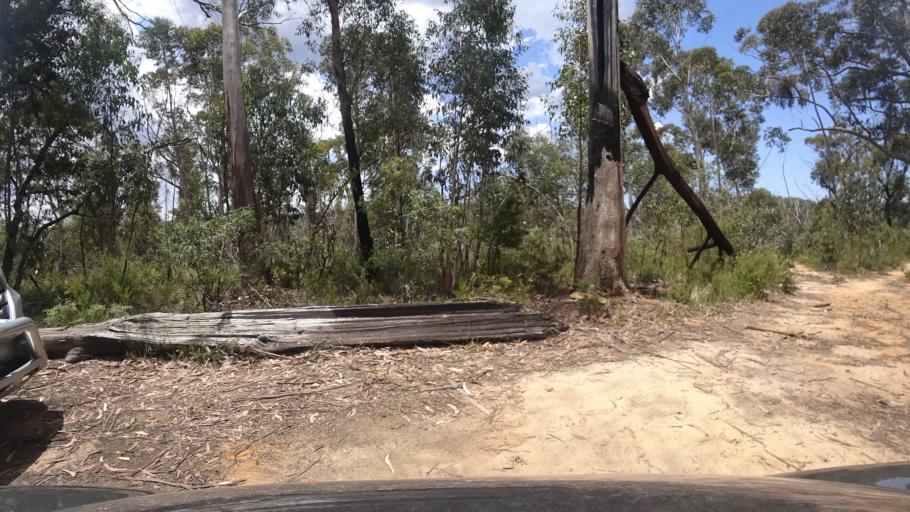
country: AU
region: New South Wales
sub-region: Lithgow
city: Lithgow
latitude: -33.4836
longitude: 150.2474
